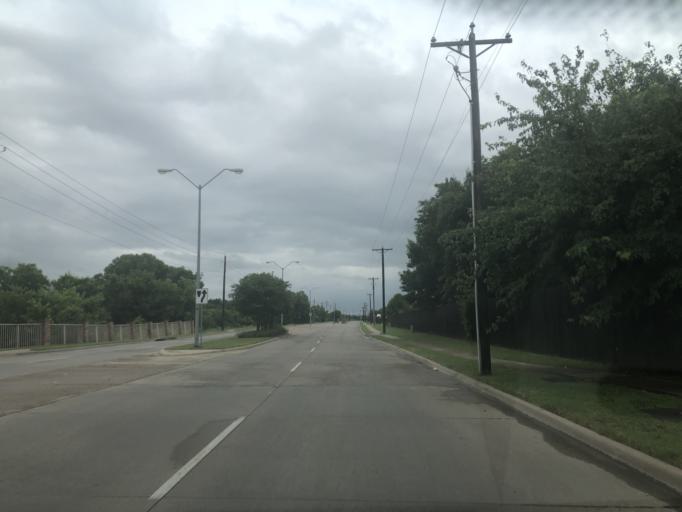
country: US
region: Texas
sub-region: Dallas County
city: Irving
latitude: 32.7909
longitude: -96.9598
